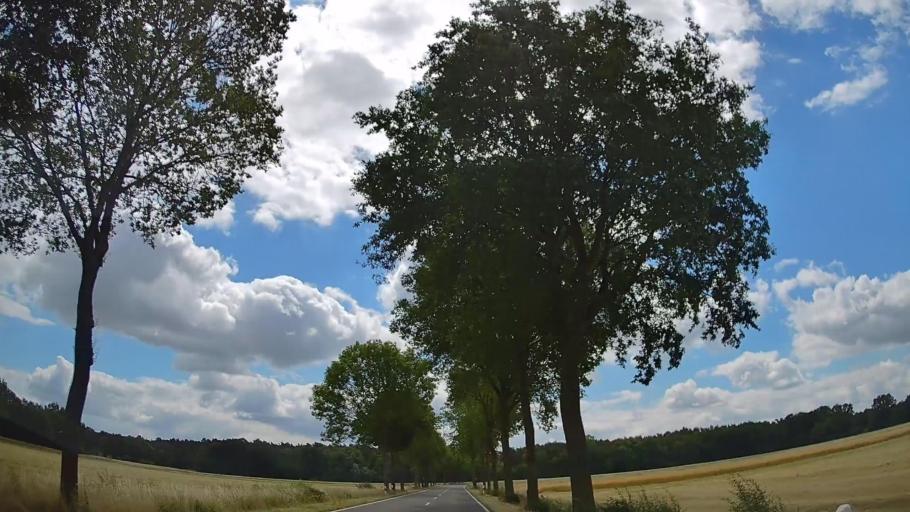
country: DE
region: North Rhine-Westphalia
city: Rahden
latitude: 52.4256
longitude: 8.5138
